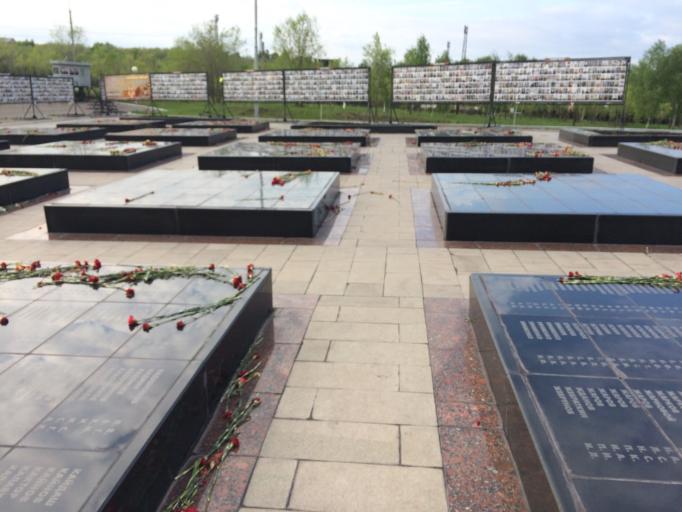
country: RU
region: Chelyabinsk
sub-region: Gorod Magnitogorsk
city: Magnitogorsk
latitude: 53.4074
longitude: 58.9916
